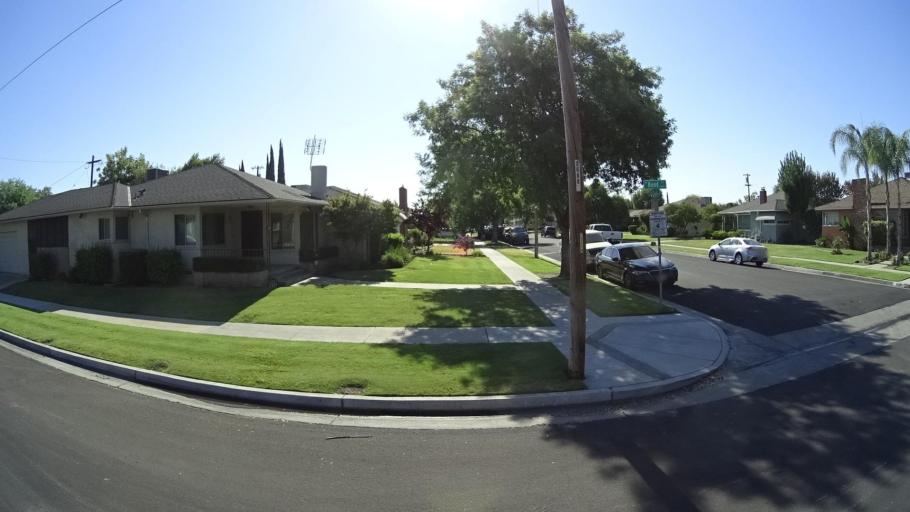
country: US
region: California
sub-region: Fresno County
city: Fresno
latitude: 36.7840
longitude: -119.7675
